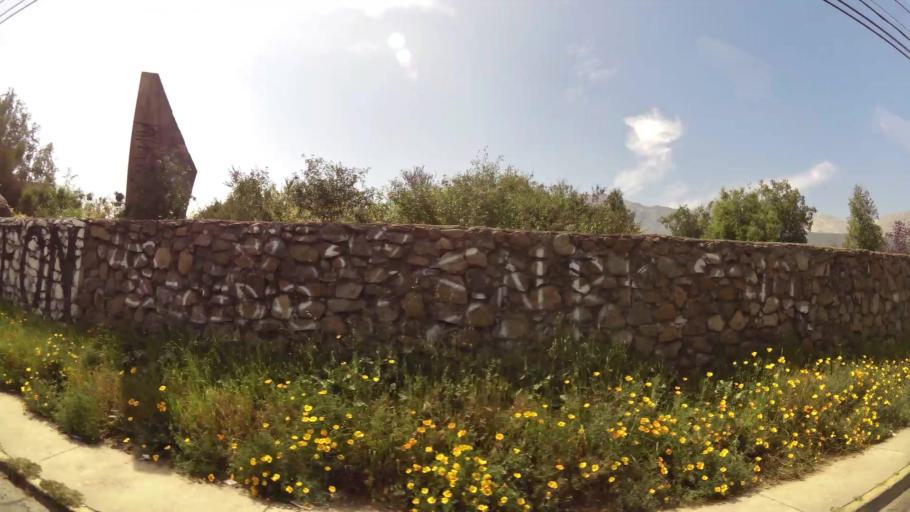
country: CL
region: Santiago Metropolitan
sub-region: Provincia de Santiago
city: Villa Presidente Frei, Nunoa, Santiago, Chile
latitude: -33.4780
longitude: -70.5250
